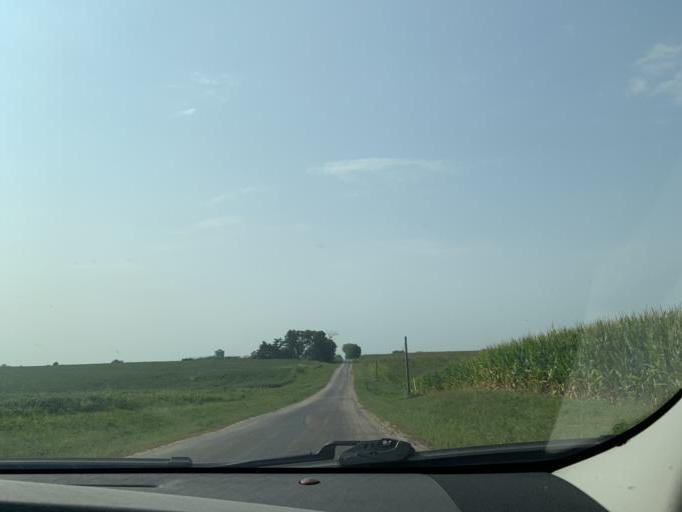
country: US
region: Illinois
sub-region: Whiteside County
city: Sterling
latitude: 41.8369
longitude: -89.7470
